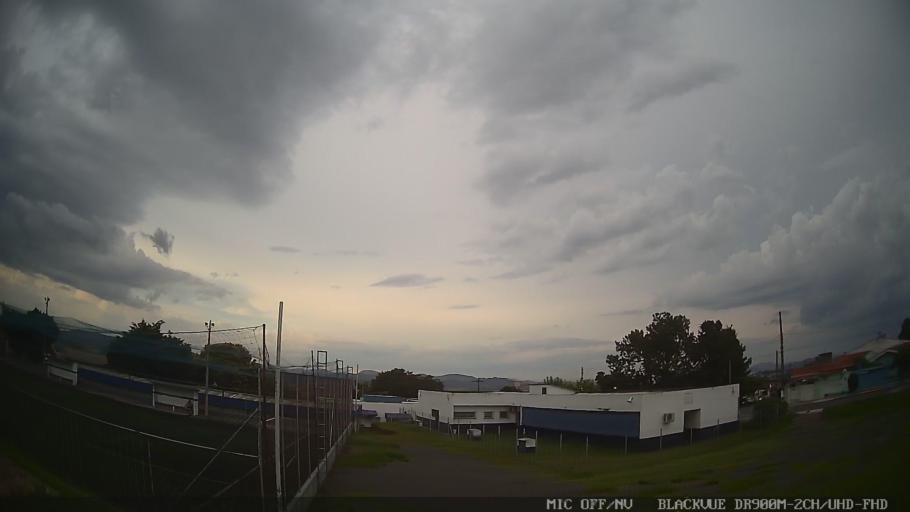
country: BR
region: Sao Paulo
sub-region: Atibaia
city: Atibaia
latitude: -23.1336
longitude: -46.5652
